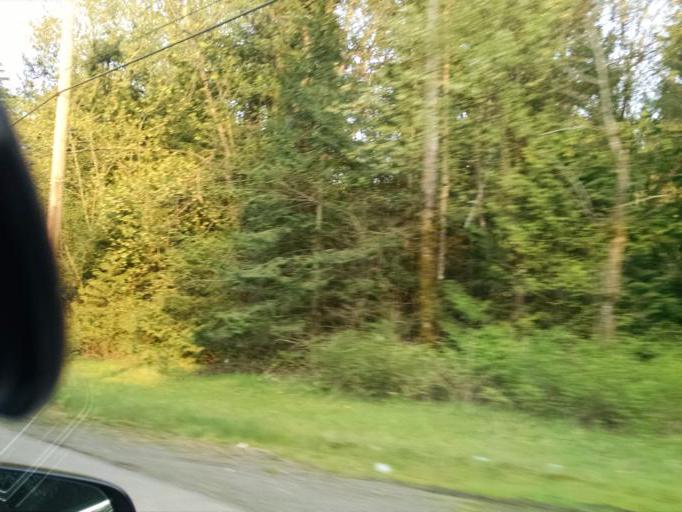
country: US
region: Washington
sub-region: Whatcom County
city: Geneva
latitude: 48.8006
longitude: -122.4035
